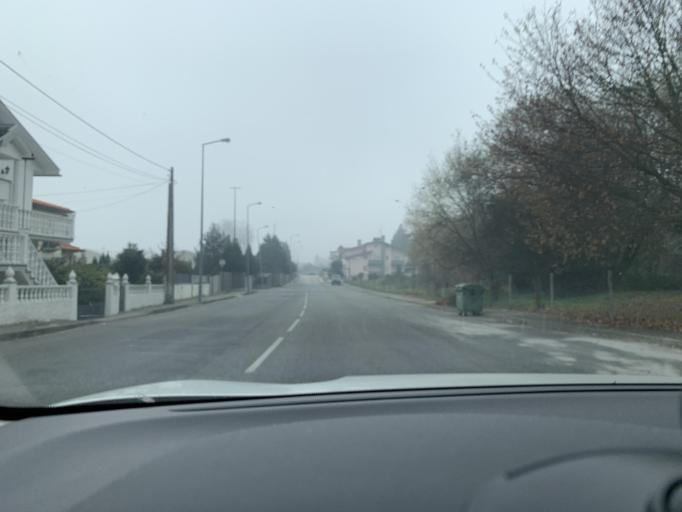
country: PT
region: Viseu
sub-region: Viseu
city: Rio de Loba
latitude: 40.6535
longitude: -7.8852
